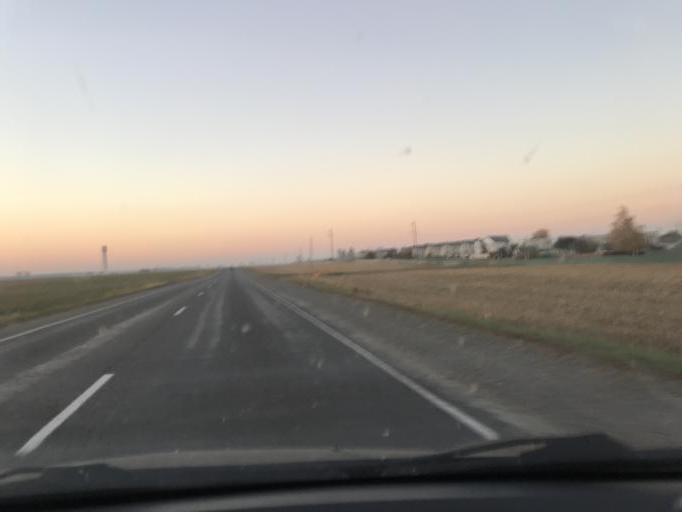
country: BY
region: Gomel
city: Horad Rechytsa
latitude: 52.2536
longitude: 30.4921
